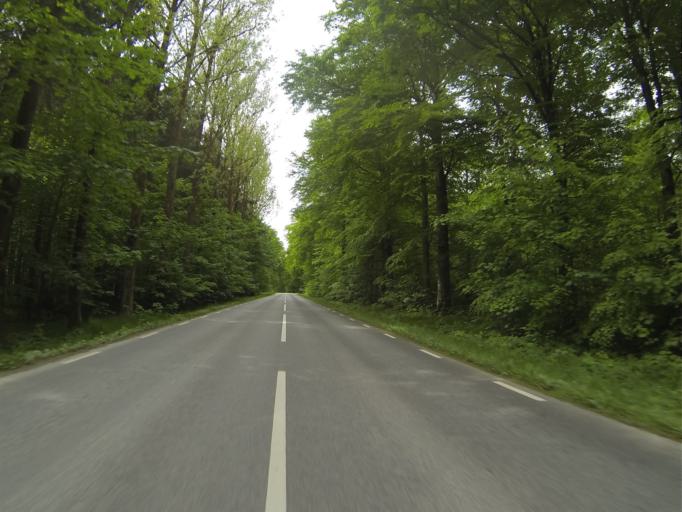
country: SE
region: Skane
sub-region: Sjobo Kommun
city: Sjoebo
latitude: 55.6625
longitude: 13.6783
